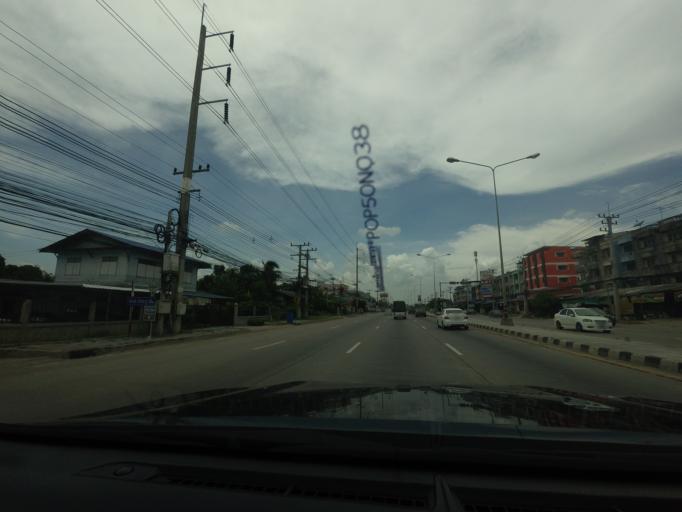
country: TH
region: Nakhon Pathom
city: Nakhon Pathom
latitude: 13.8522
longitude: 100.0180
